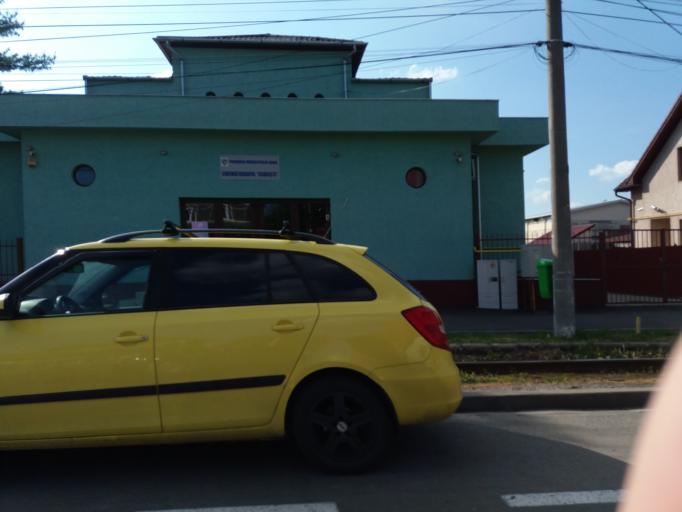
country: RO
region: Arad
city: Arad
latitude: 46.1940
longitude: 21.3328
